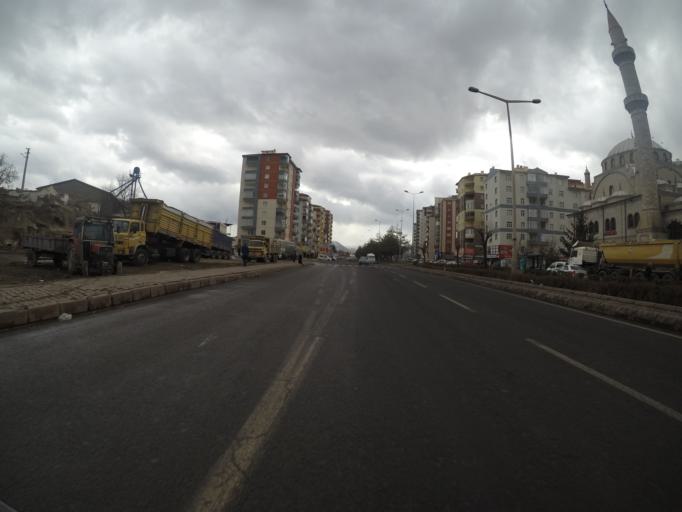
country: TR
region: Kayseri
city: Melikgazi
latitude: 38.7537
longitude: 35.4690
